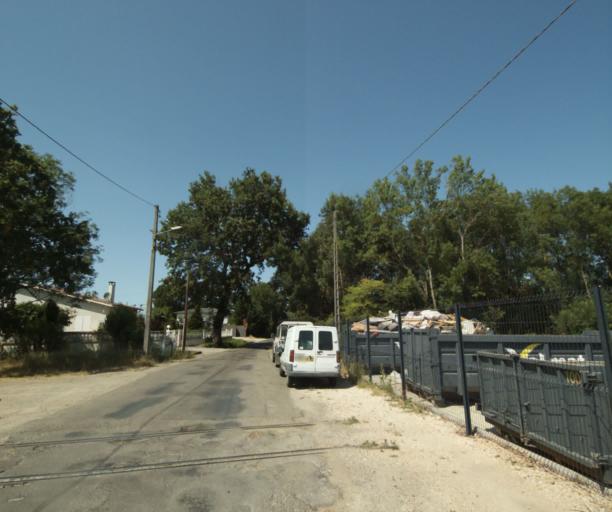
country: FR
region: Midi-Pyrenees
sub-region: Departement du Tarn-et-Garonne
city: Montauban
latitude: 44.0417
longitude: 1.3633
